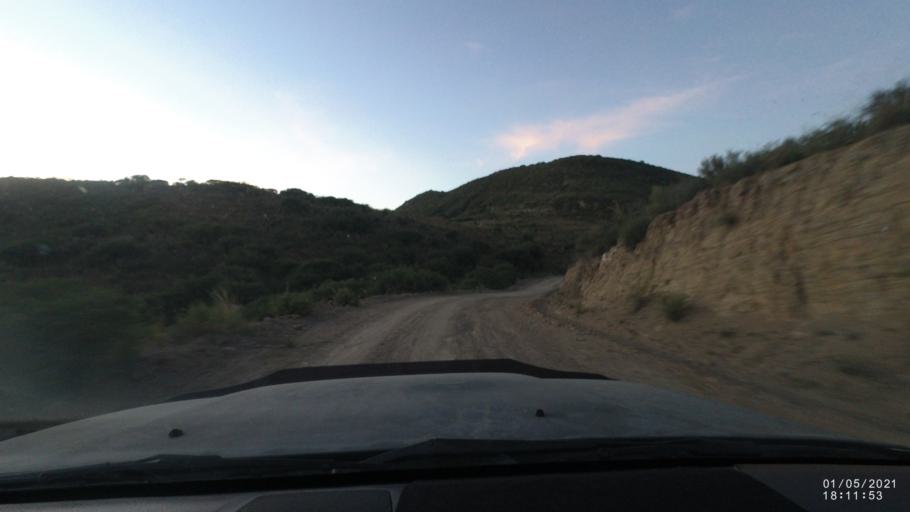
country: BO
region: Cochabamba
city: Capinota
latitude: -17.6799
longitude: -66.2012
